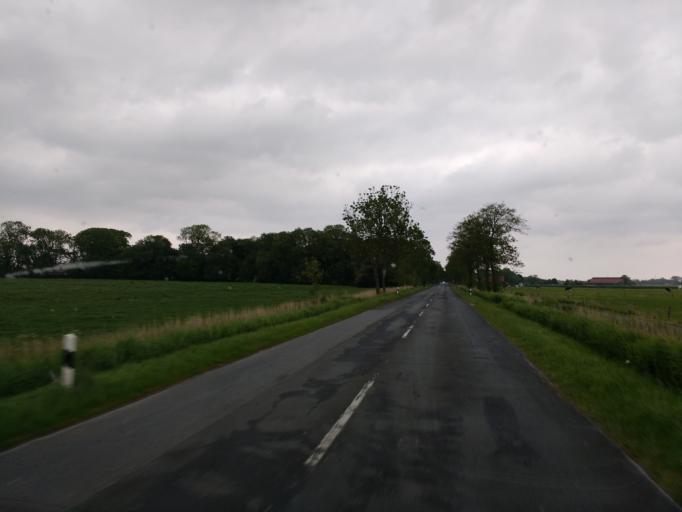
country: DE
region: Lower Saxony
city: Schillig
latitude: 53.6675
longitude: 7.9410
